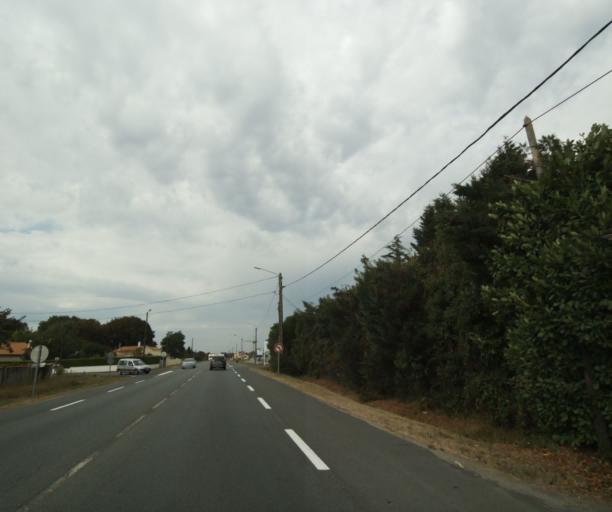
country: FR
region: Poitou-Charentes
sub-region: Departement de la Charente-Maritime
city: Tonnay-Charente
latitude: 45.9495
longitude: -0.9012
